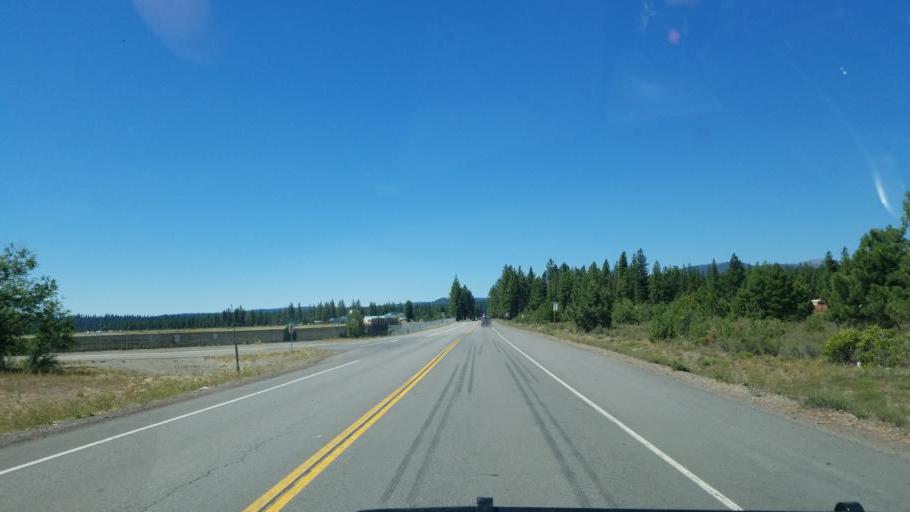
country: US
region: California
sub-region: Plumas County
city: Chester
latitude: 40.2933
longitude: -121.2422
